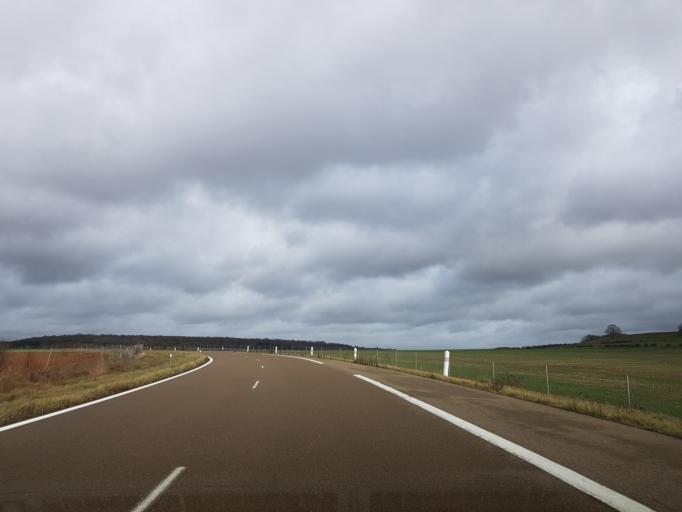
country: FR
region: Champagne-Ardenne
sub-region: Departement de la Haute-Marne
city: Rolampont
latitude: 47.9103
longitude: 5.2275
